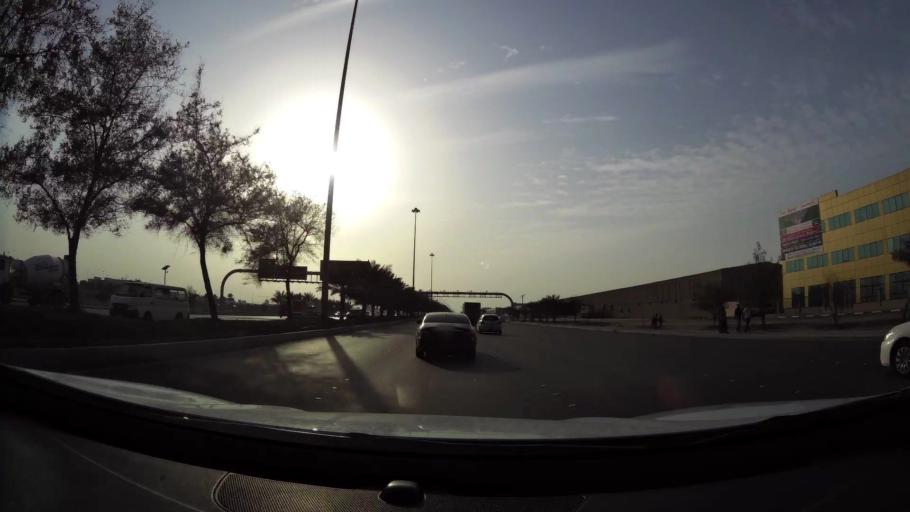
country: AE
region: Abu Dhabi
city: Abu Dhabi
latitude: 24.3467
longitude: 54.5210
